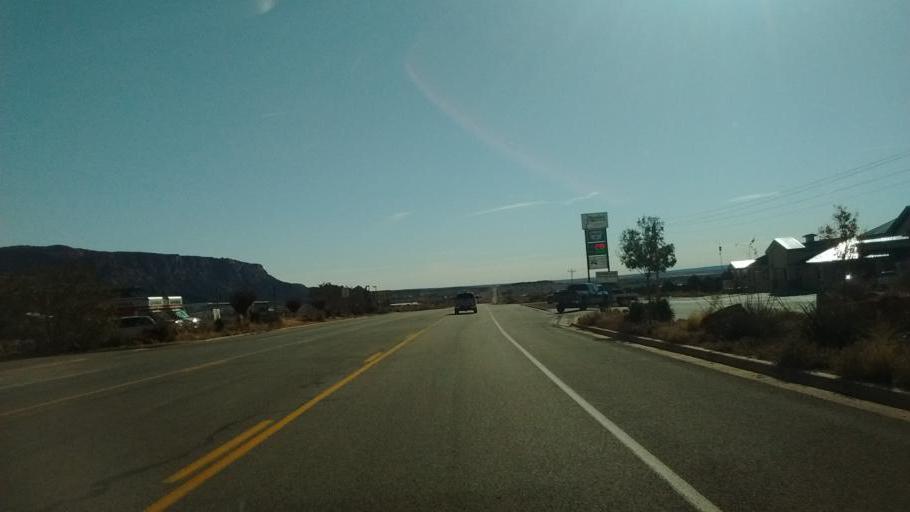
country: US
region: Arizona
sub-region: Mohave County
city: Colorado City
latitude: 37.0014
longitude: -112.9999
